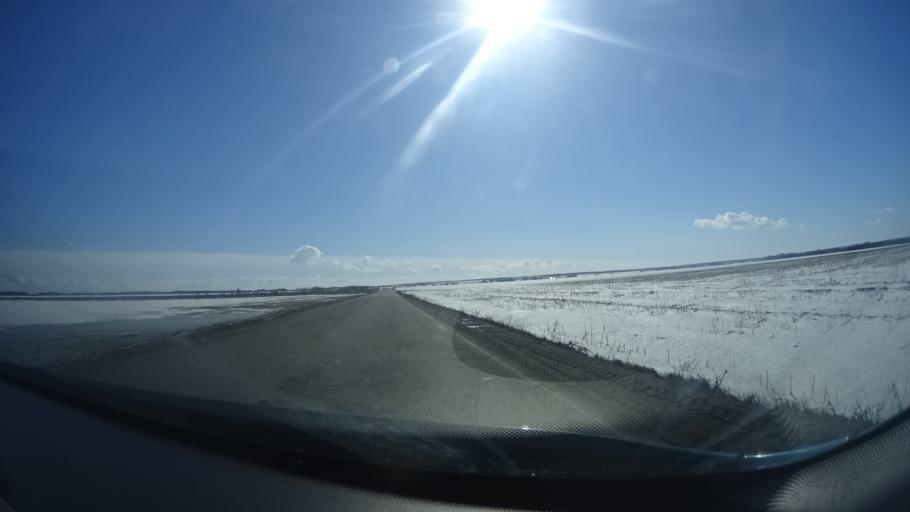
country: RU
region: Bashkortostan
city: Avdon
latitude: 54.5982
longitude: 55.8512
